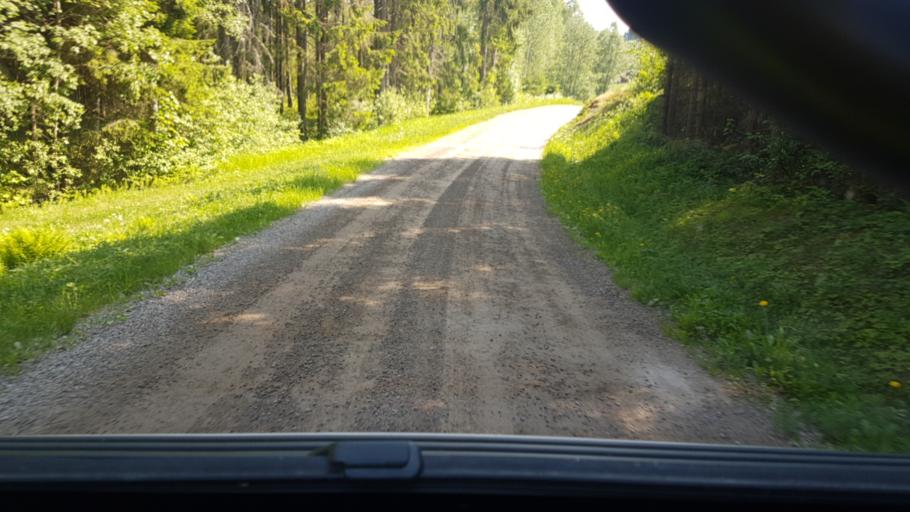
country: SE
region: Vaermland
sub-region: Eda Kommun
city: Amotfors
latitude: 59.7905
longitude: 12.4281
